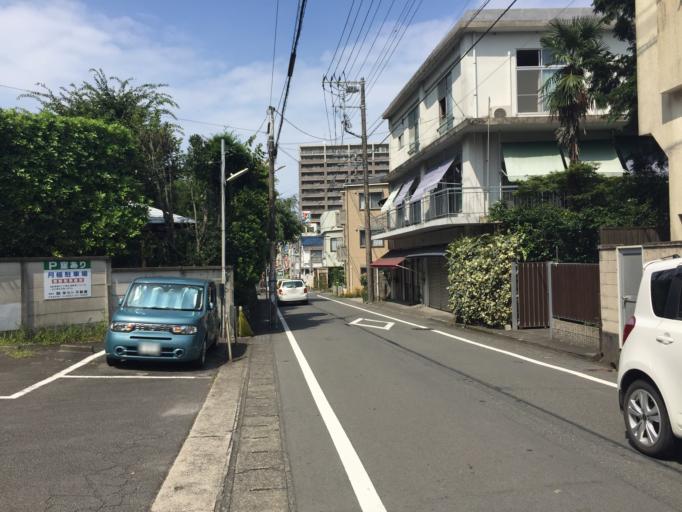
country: JP
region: Shizuoka
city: Ito
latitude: 34.9711
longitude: 139.0915
